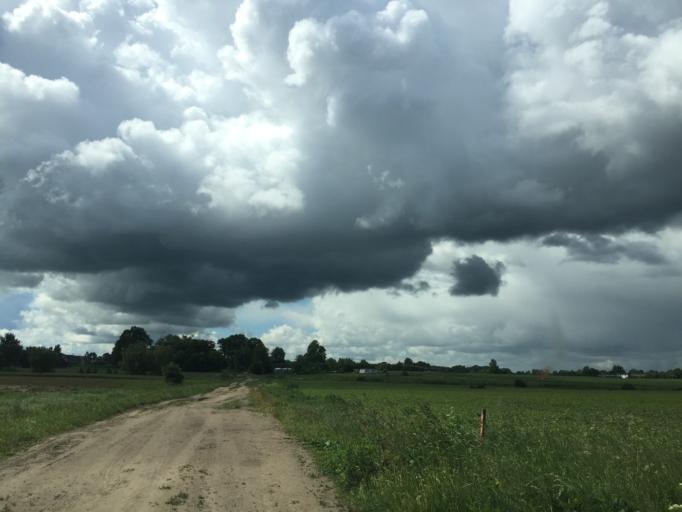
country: LV
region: Lecava
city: Iecava
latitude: 56.6110
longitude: 24.2038
